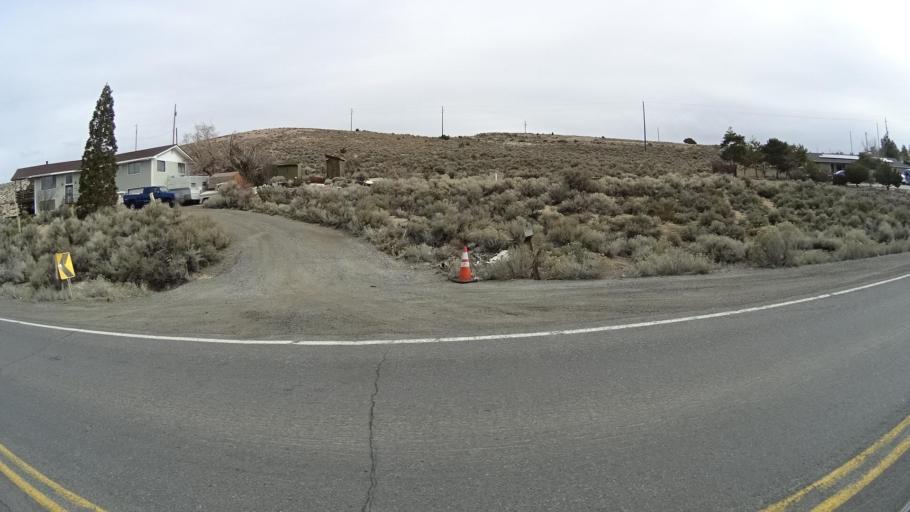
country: US
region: Nevada
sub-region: Washoe County
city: Golden Valley
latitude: 39.6056
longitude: -119.8098
